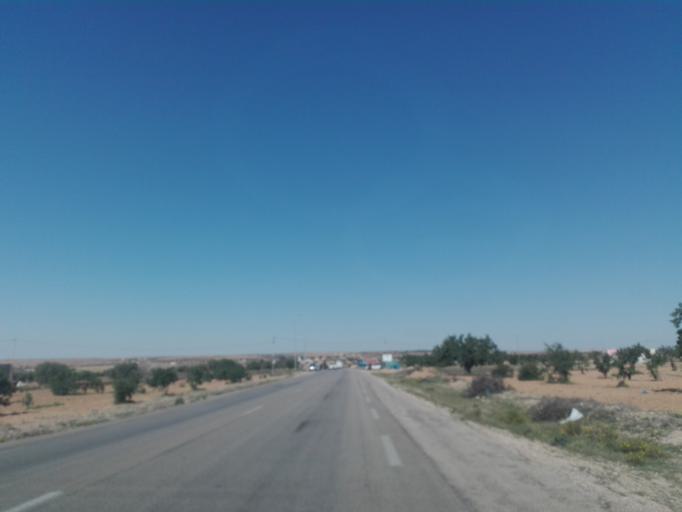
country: TN
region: Safaqis
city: Bi'r `Ali Bin Khalifah
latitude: 34.7407
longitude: 10.3891
